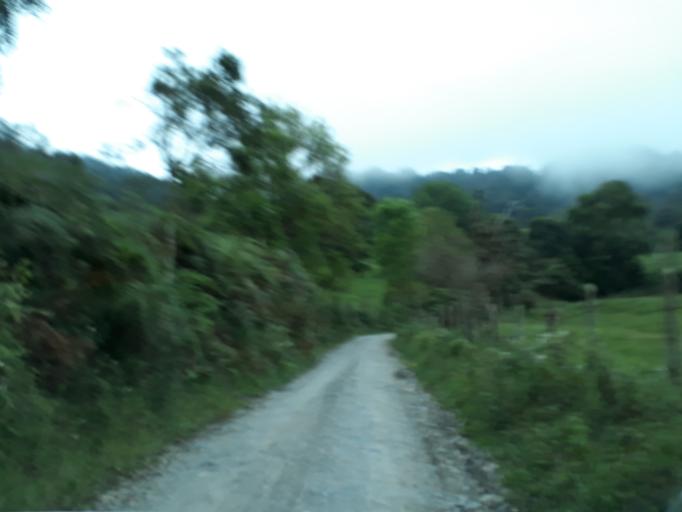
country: CO
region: Boyaca
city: Muzo
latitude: 5.3773
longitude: -74.0729
